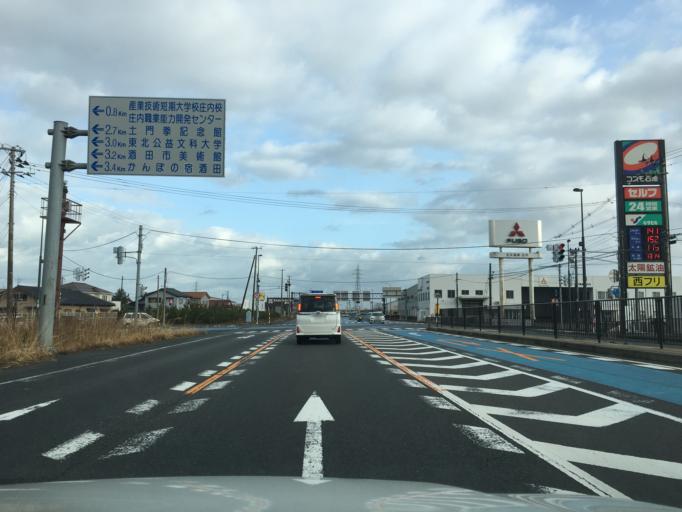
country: JP
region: Yamagata
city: Sakata
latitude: 38.8802
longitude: 139.8385
